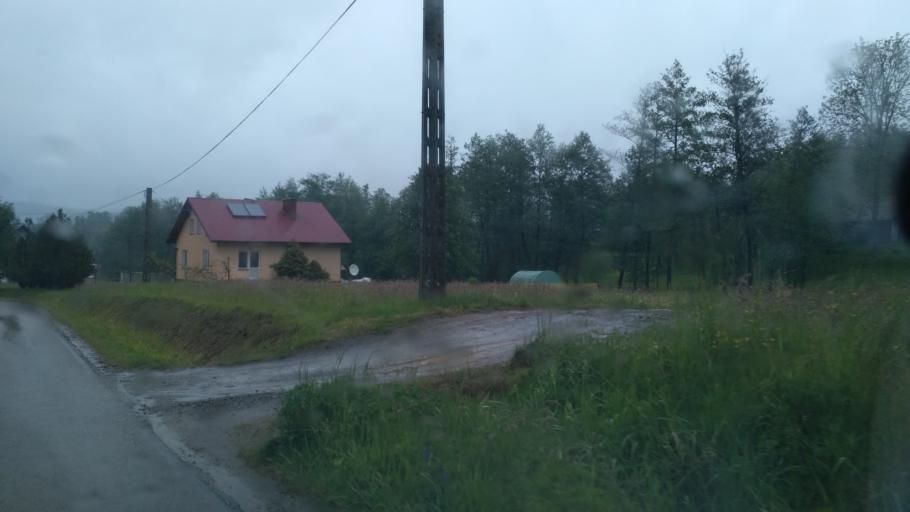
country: PL
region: Subcarpathian Voivodeship
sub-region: Powiat jasielski
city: Jaslo
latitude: 49.7950
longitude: 21.4916
